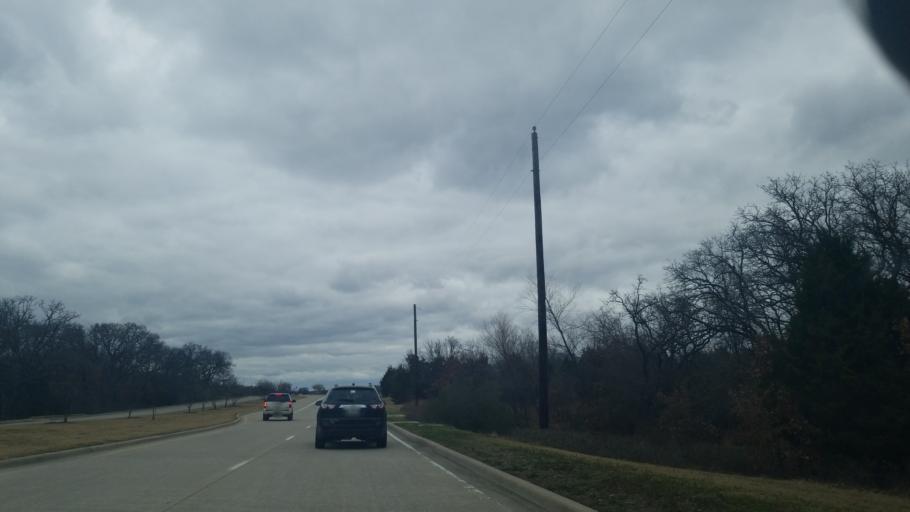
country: US
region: Texas
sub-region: Denton County
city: Copper Canyon
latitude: 33.1083
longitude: -97.0788
